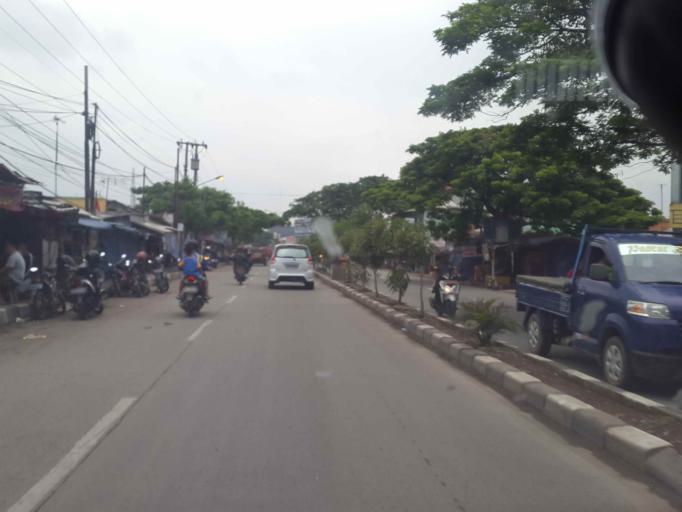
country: ID
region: West Java
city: Cikarang
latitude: -6.2896
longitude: 107.1525
